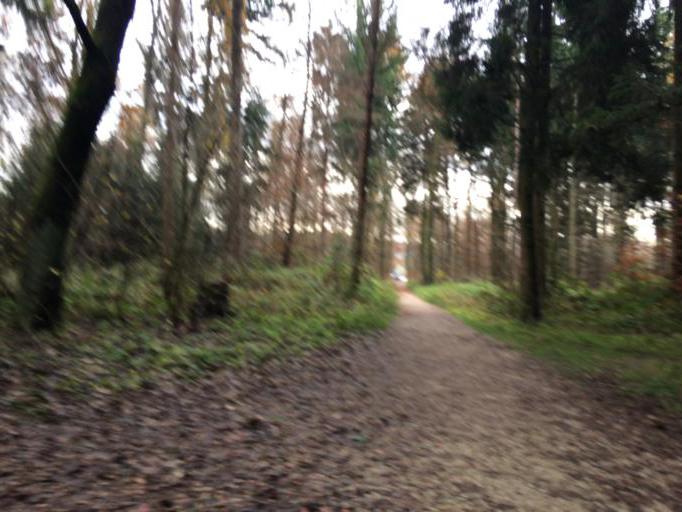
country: CH
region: Bern
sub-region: Bern-Mittelland District
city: Bern
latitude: 46.9551
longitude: 7.4207
